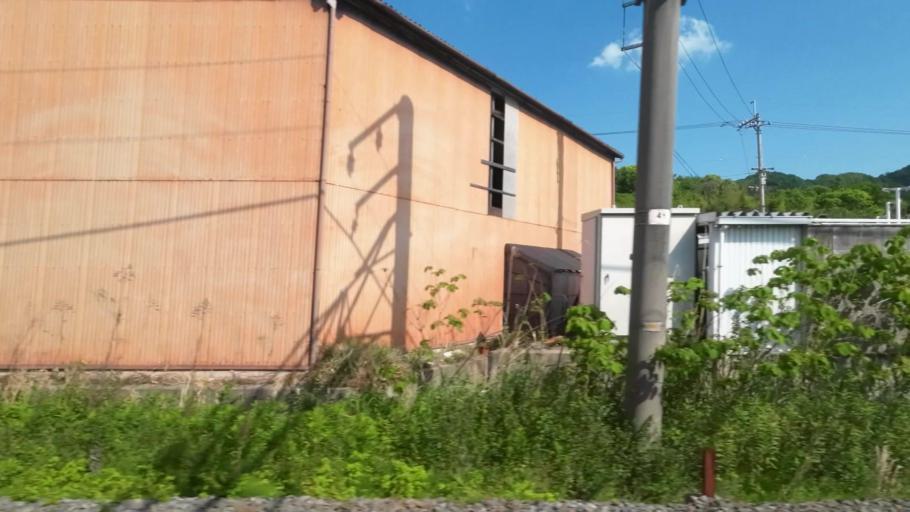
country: JP
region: Kagawa
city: Takamatsu-shi
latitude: 34.3082
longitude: 133.9758
